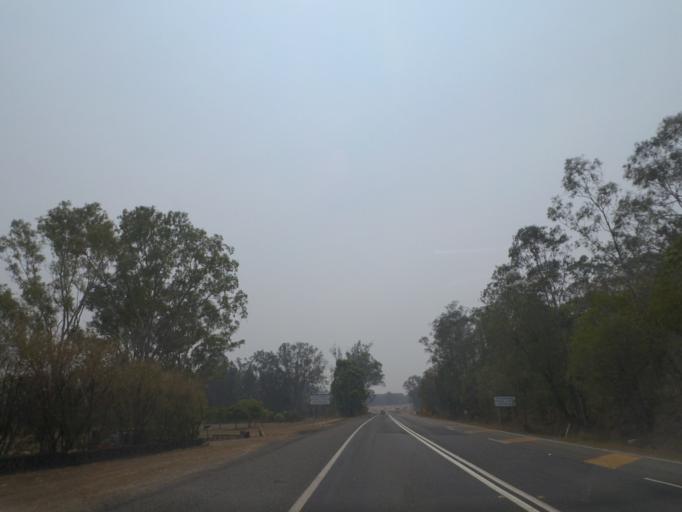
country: AU
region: New South Wales
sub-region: Clarence Valley
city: Maclean
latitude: -29.5531
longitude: 153.1534
